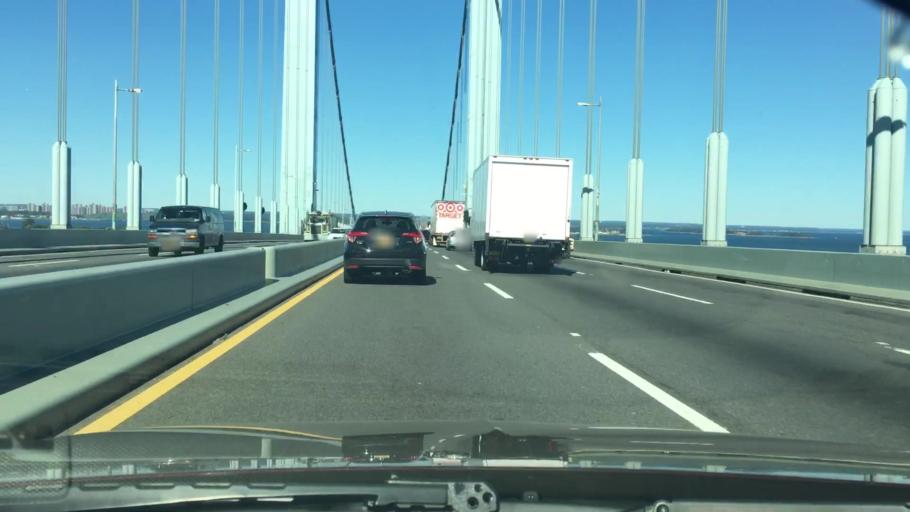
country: US
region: New York
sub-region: Nassau County
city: East Atlantic Beach
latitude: 40.8014
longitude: -73.7937
